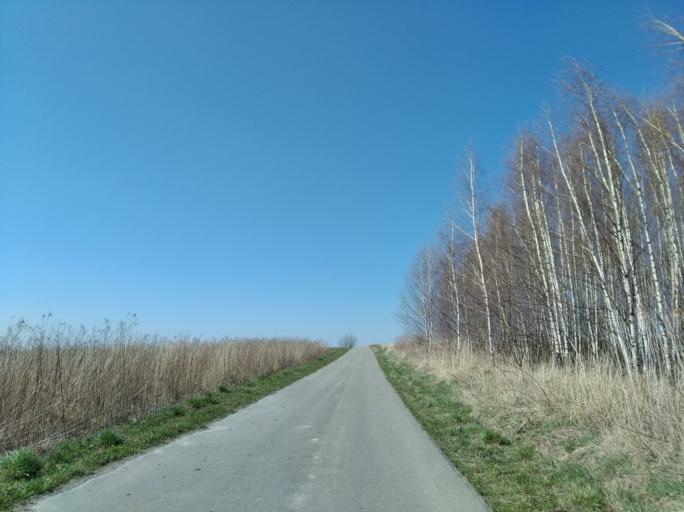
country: PL
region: Subcarpathian Voivodeship
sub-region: Powiat strzyzowski
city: Strzyzow
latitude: 49.8643
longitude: 21.8419
